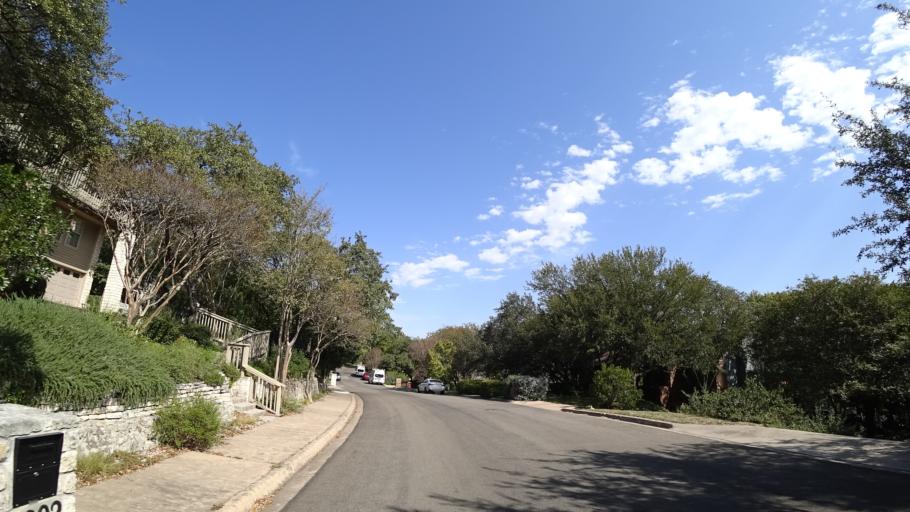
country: US
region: Texas
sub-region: Travis County
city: West Lake Hills
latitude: 30.3459
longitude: -97.7670
